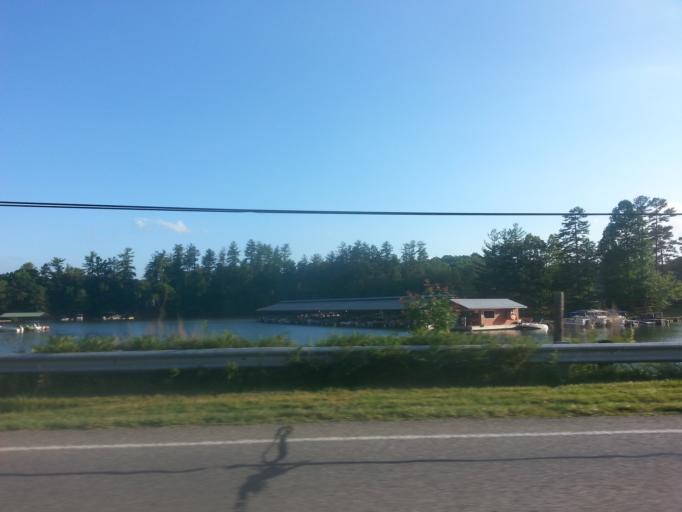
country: US
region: Georgia
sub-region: Union County
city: Blairsville
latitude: 34.8967
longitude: -84.0015
